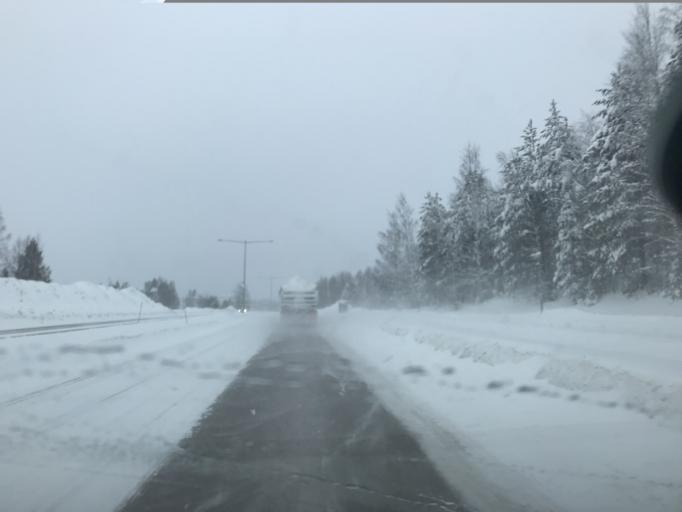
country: SE
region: Norrbotten
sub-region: Lulea Kommun
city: Lulea
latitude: 65.6082
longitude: 22.1378
